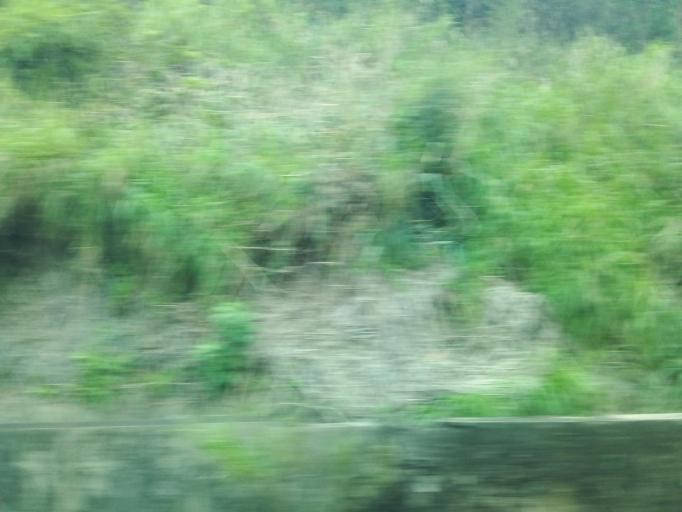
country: BR
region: Minas Gerais
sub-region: Joao Monlevade
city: Joao Monlevade
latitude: -19.8305
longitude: -43.1277
